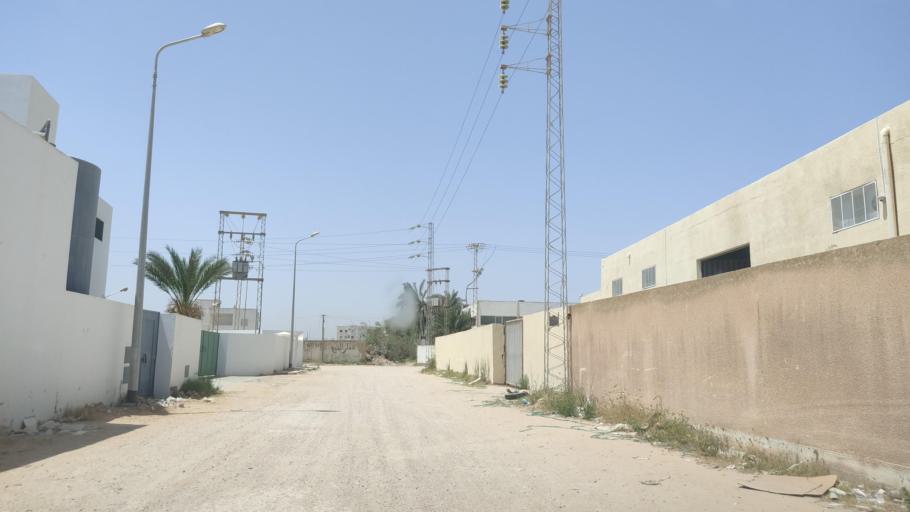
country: TN
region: Safaqis
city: Sfax
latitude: 34.7090
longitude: 10.7280
